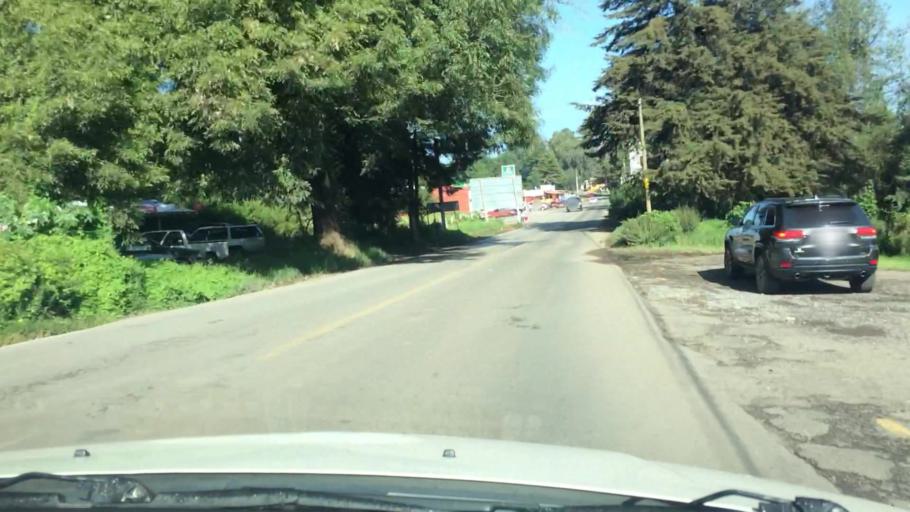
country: MX
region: Mexico
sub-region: Valle de Bravo
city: Cuadrilla de Dolores
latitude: 19.1464
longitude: -100.0689
